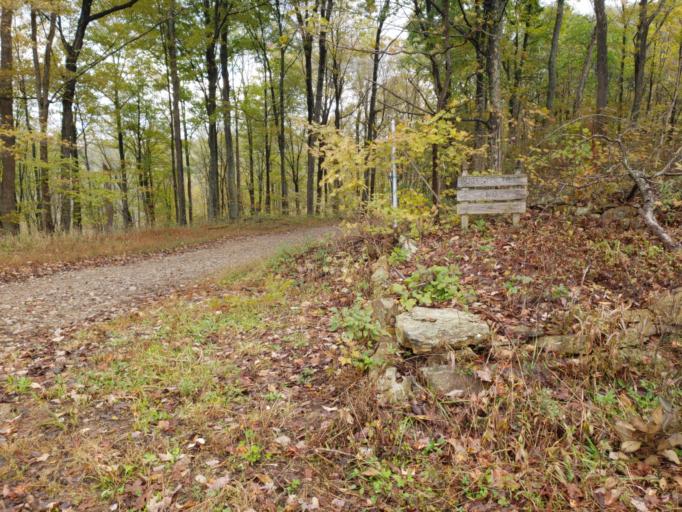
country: US
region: Ohio
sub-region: Vinton County
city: McArthur
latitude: 39.3481
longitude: -82.6660
